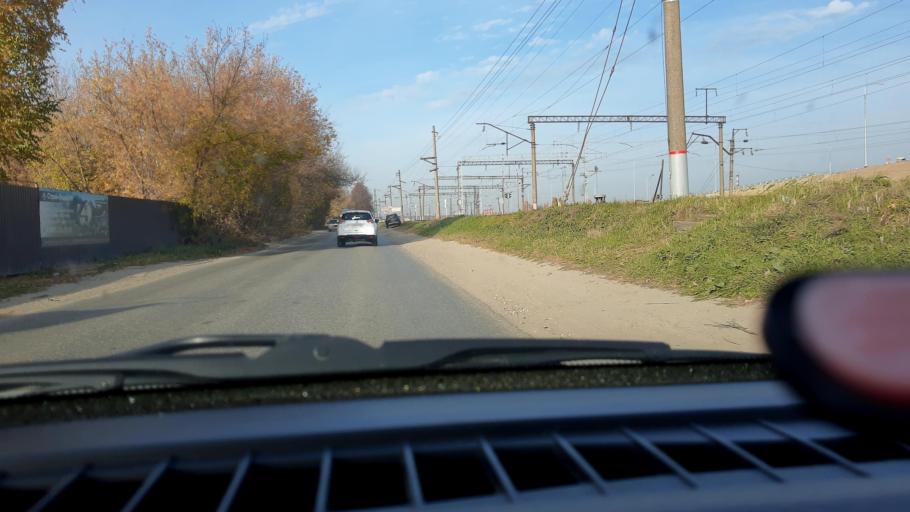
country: RU
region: Nizjnij Novgorod
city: Neklyudovo
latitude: 56.4030
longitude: 43.9817
